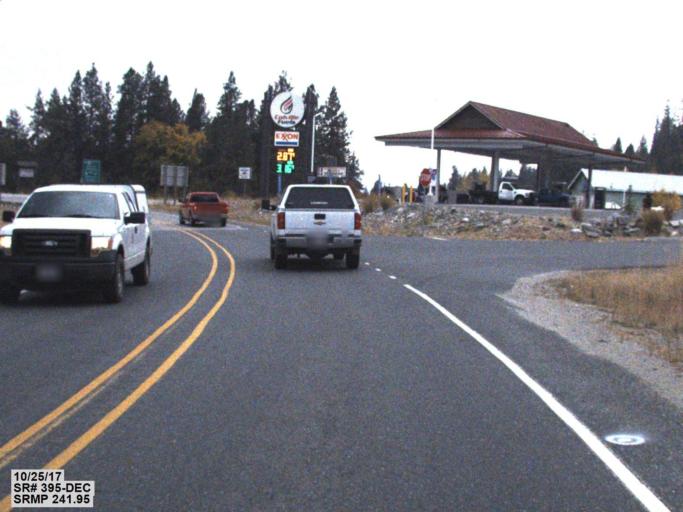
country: US
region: Washington
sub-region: Stevens County
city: Kettle Falls
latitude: 48.6283
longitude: -118.1229
